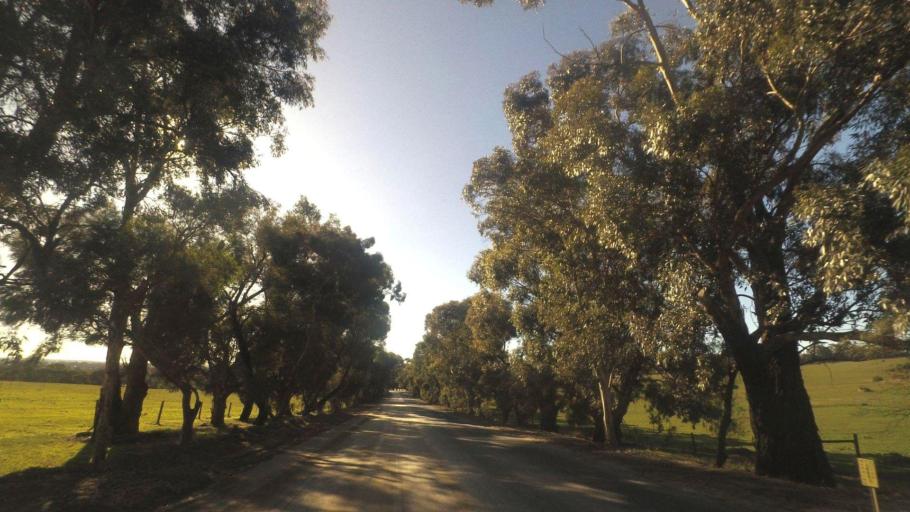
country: AU
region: Victoria
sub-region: Knox
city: Rowville
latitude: -37.9318
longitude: 145.2620
